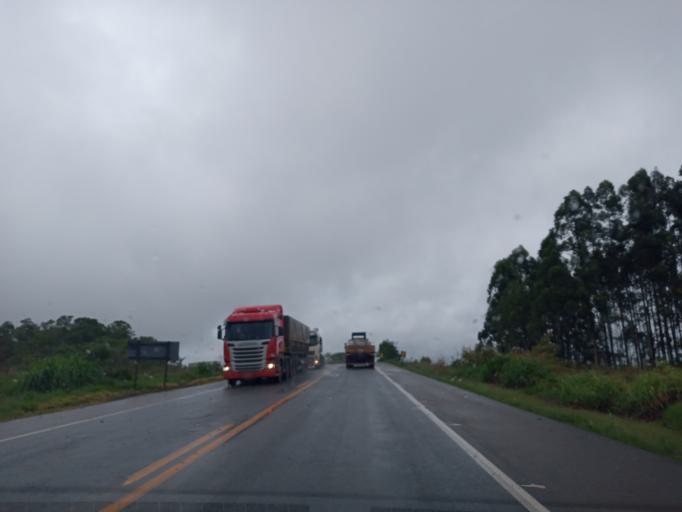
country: BR
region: Minas Gerais
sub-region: Campos Altos
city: Campos Altos
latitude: -19.7385
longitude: -46.0083
